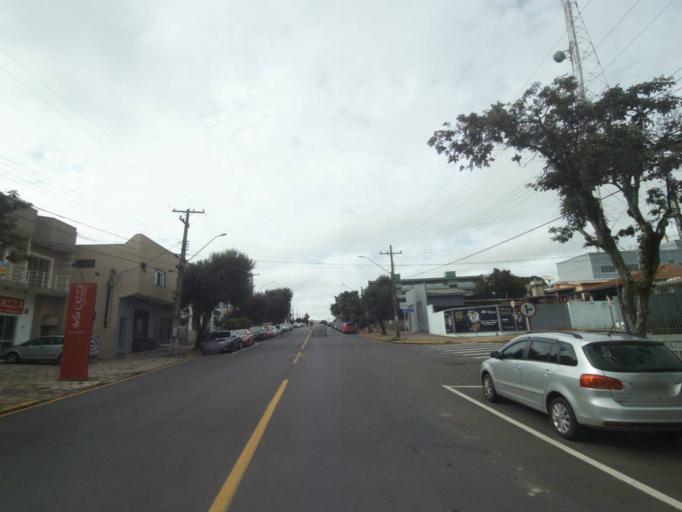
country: BR
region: Parana
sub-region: Telemaco Borba
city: Telemaco Borba
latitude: -24.3276
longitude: -50.6164
